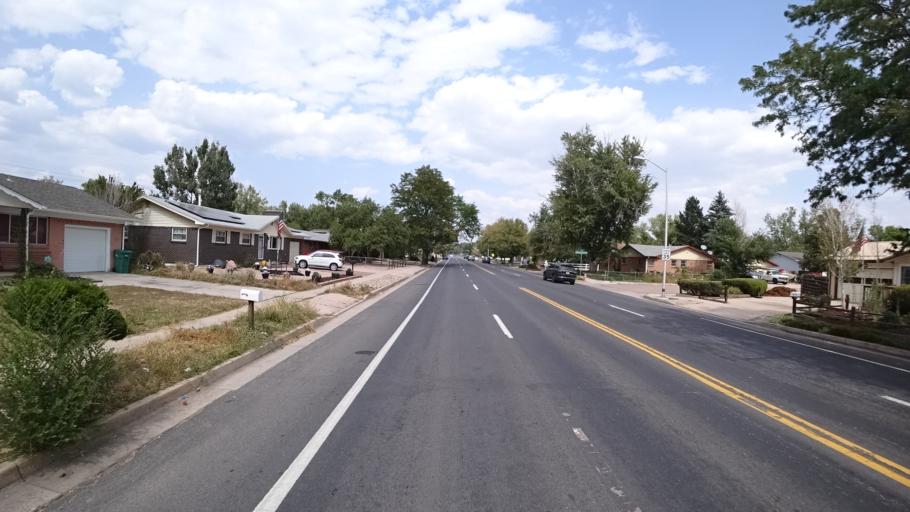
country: US
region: Colorado
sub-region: El Paso County
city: Cimarron Hills
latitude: 38.8481
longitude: -104.7481
